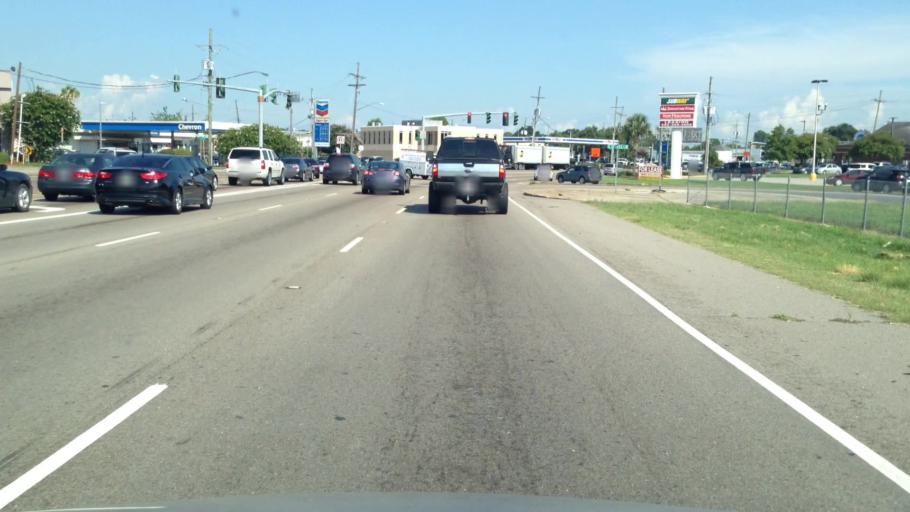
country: US
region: Louisiana
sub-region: Jefferson Parish
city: Metairie Terrace
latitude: 29.9957
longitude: -90.1831
